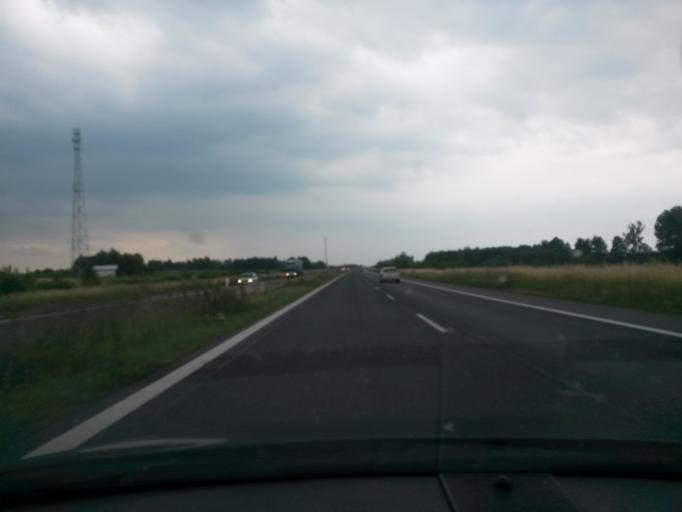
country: PL
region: Silesian Voivodeship
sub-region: Powiat czestochowski
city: Borowno
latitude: 50.9751
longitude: 19.2712
